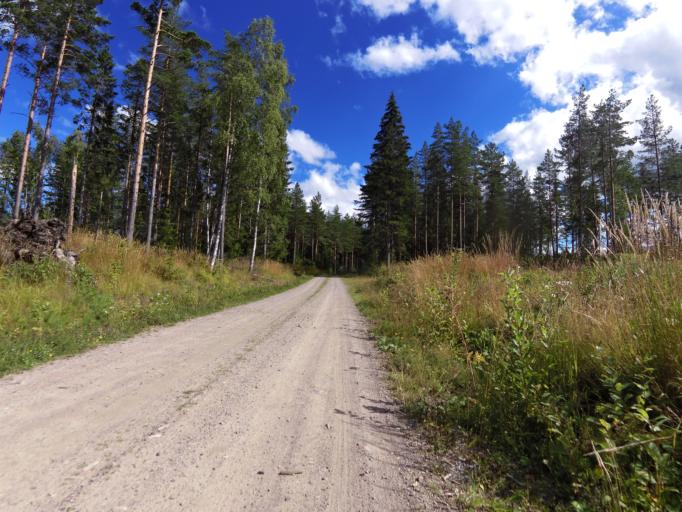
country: SE
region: Gaevleborg
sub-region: Hofors Kommun
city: Hofors
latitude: 60.5248
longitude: 16.2355
